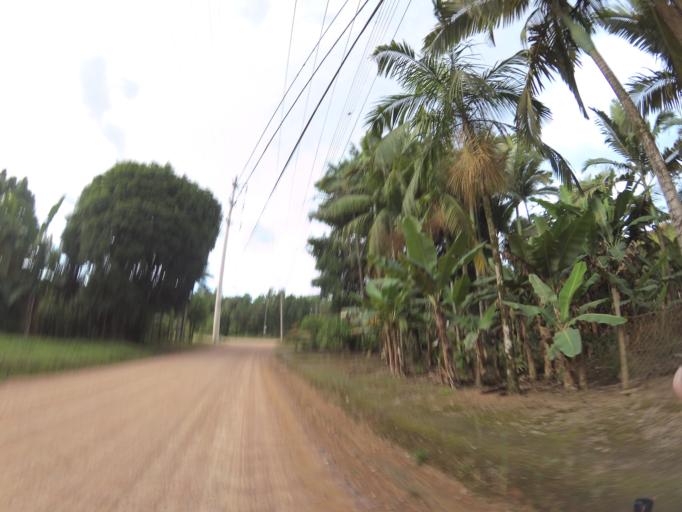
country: BR
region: Santa Catarina
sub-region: Pomerode
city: Pomerode
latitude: -26.7728
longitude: -49.1639
